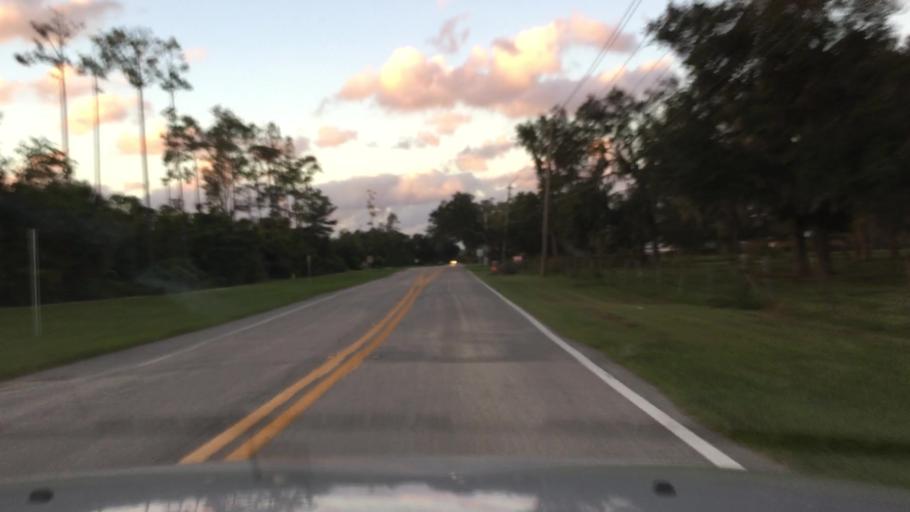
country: US
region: Florida
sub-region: Volusia County
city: Ormond Beach
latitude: 29.2779
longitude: -81.1129
